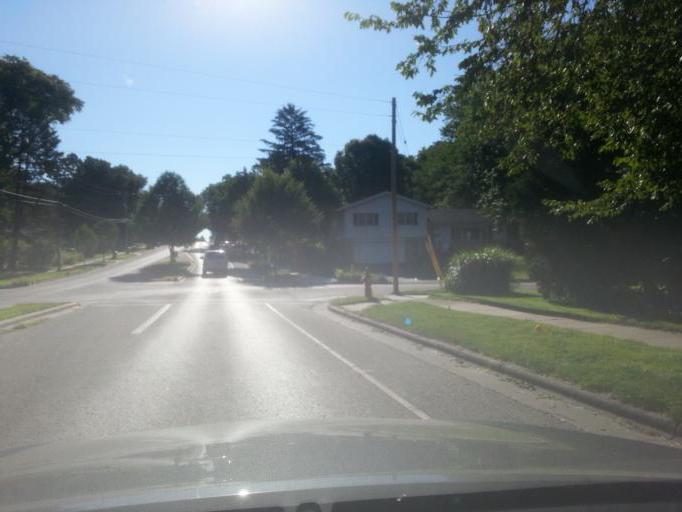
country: US
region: Wisconsin
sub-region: Dane County
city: Shorewood Hills
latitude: 43.0500
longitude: -89.4677
